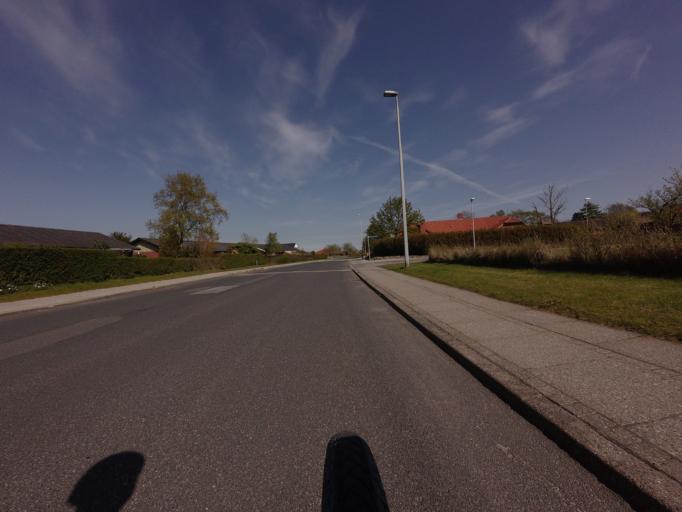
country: DK
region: North Denmark
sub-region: Jammerbugt Kommune
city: Pandrup
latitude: 57.2217
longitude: 9.6671
